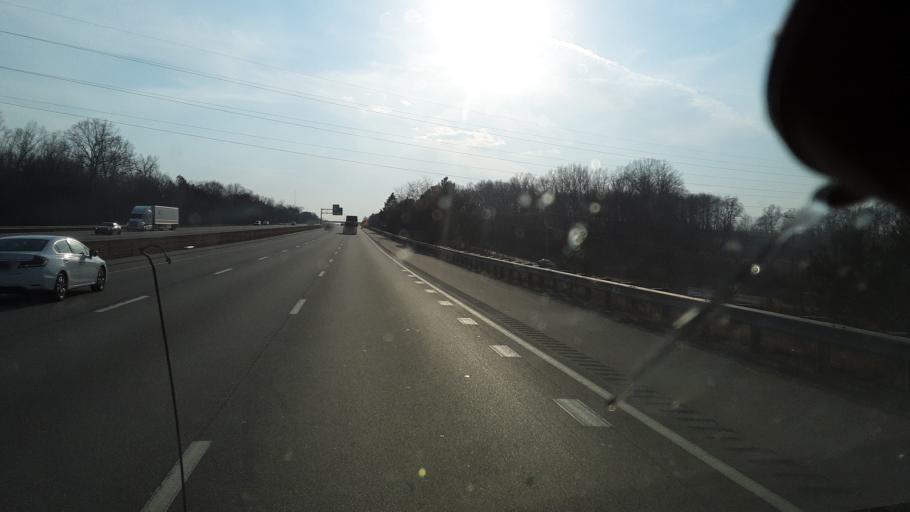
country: US
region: Ohio
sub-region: Trumbull County
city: McDonald
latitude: 41.1390
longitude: -80.7278
